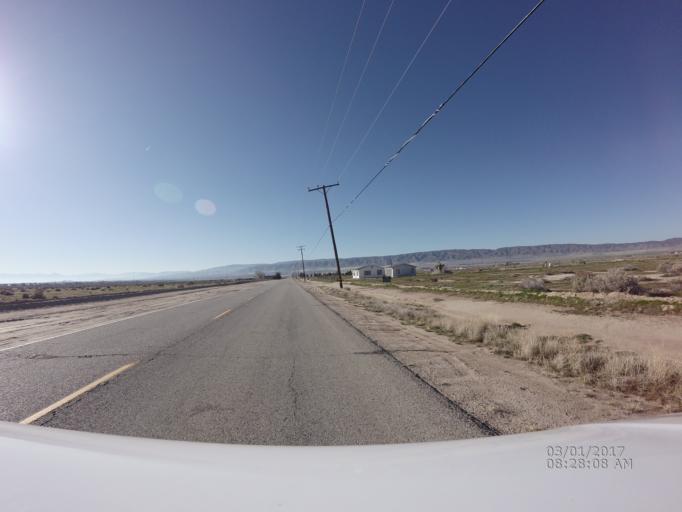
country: US
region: California
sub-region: Los Angeles County
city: Quartz Hill
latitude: 34.6958
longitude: -118.2543
